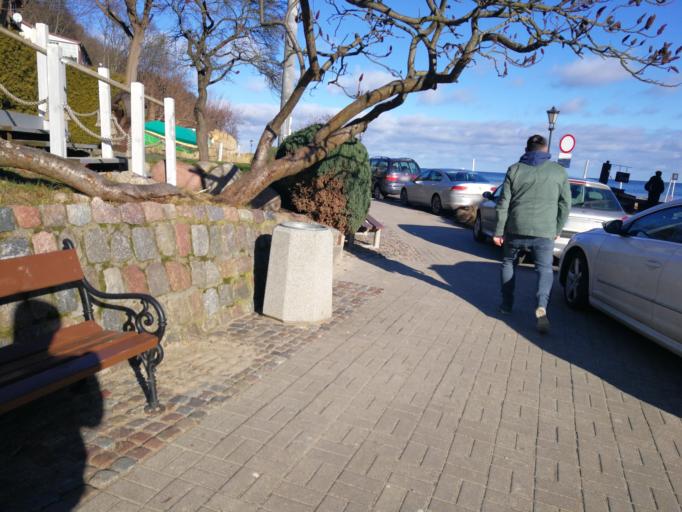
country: PL
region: Pomeranian Voivodeship
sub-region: Sopot
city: Sopot
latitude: 54.4815
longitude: 18.5643
